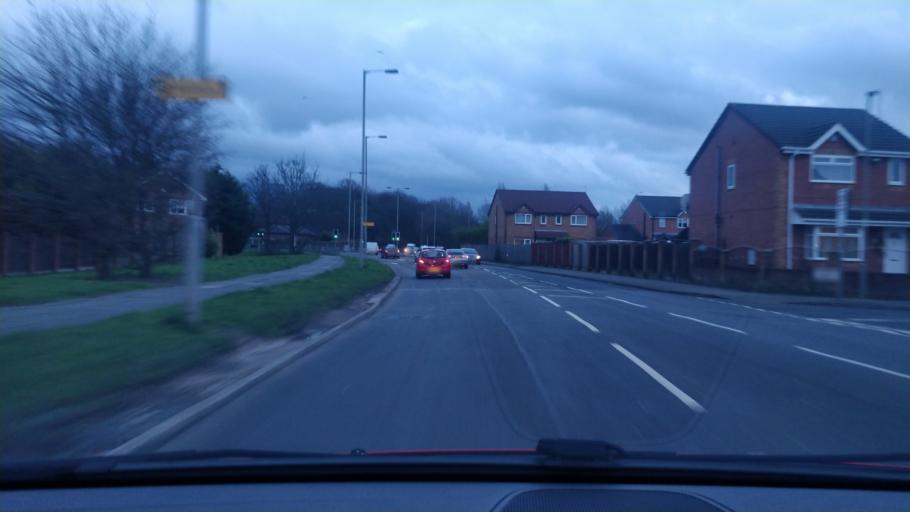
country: GB
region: England
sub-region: Knowsley
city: Kirkby
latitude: 53.4472
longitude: -2.9006
